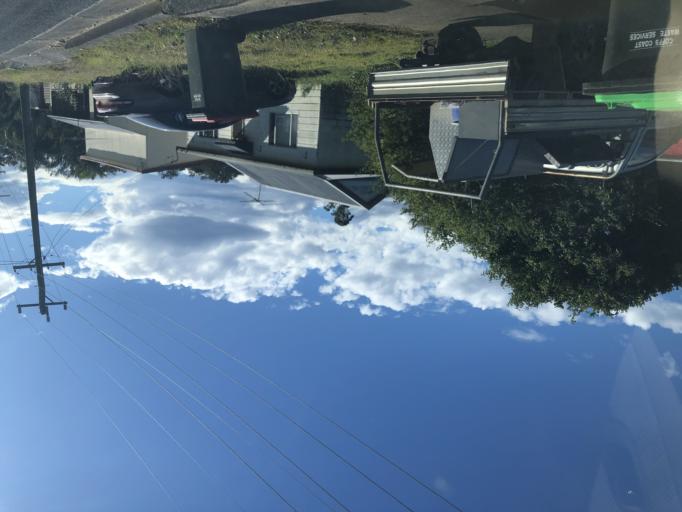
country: AU
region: New South Wales
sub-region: Nambucca Shire
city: Bowraville
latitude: -30.6483
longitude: 152.8512
